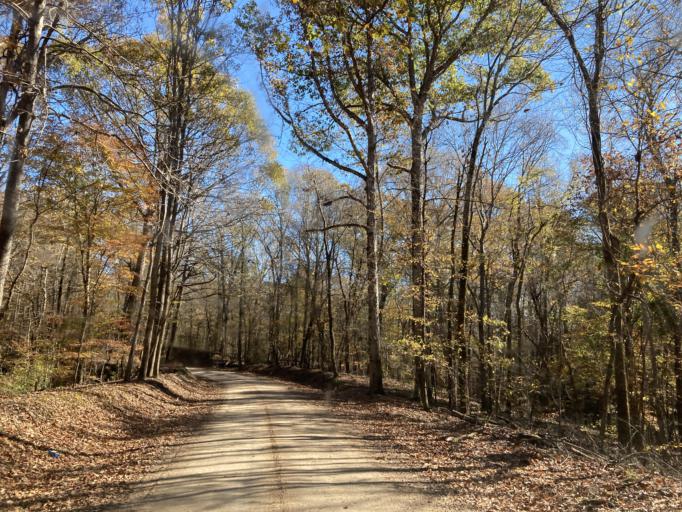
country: US
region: Mississippi
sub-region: Madison County
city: Kearney Park
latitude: 32.6682
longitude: -90.5115
